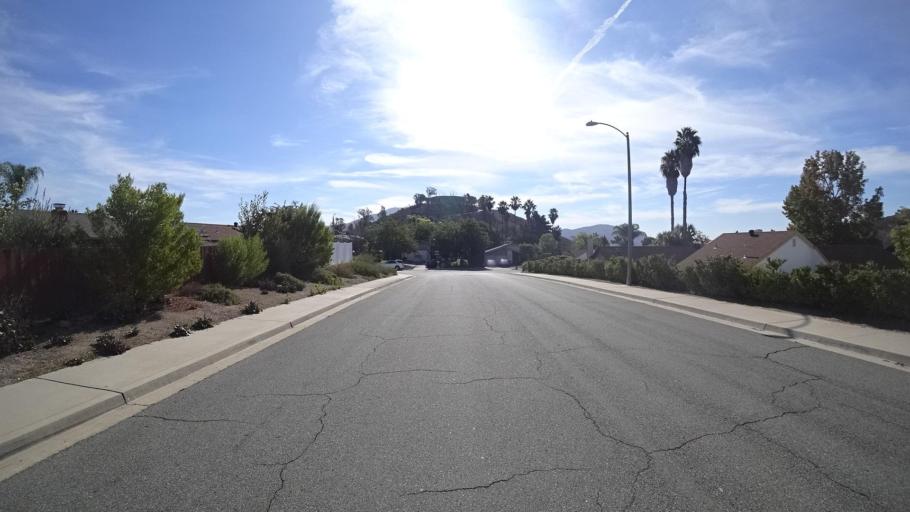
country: US
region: California
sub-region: San Diego County
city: Spring Valley
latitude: 32.7291
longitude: -116.9815
